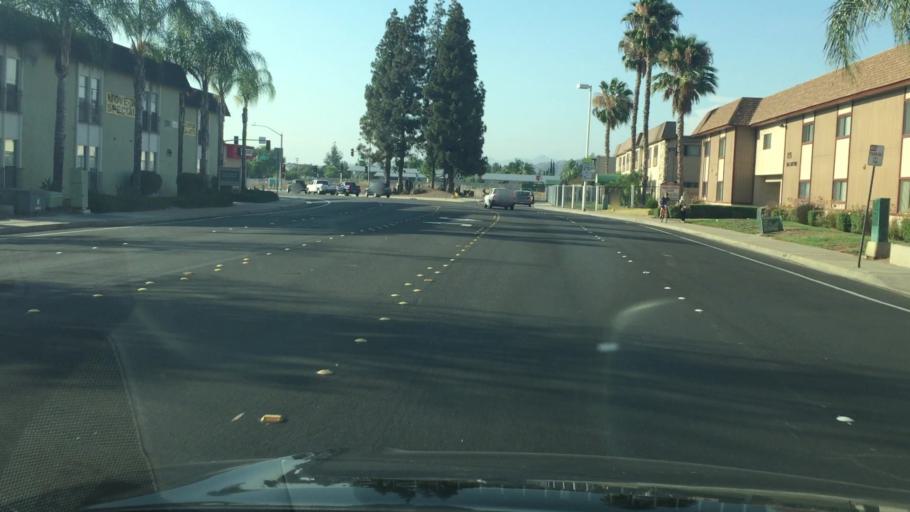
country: US
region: California
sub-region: San Diego County
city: El Cajon
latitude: 32.7969
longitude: -116.9573
